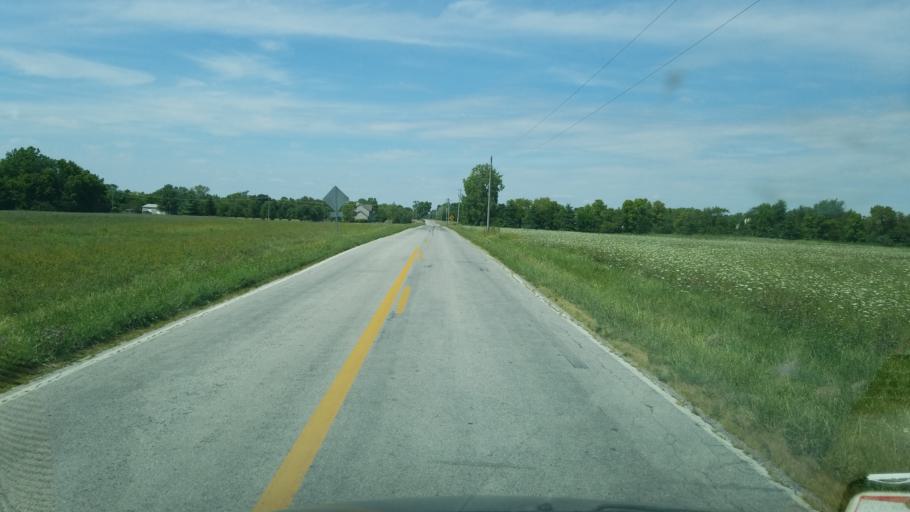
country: US
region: Ohio
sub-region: Marion County
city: Prospect
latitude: 40.3473
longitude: -83.1770
